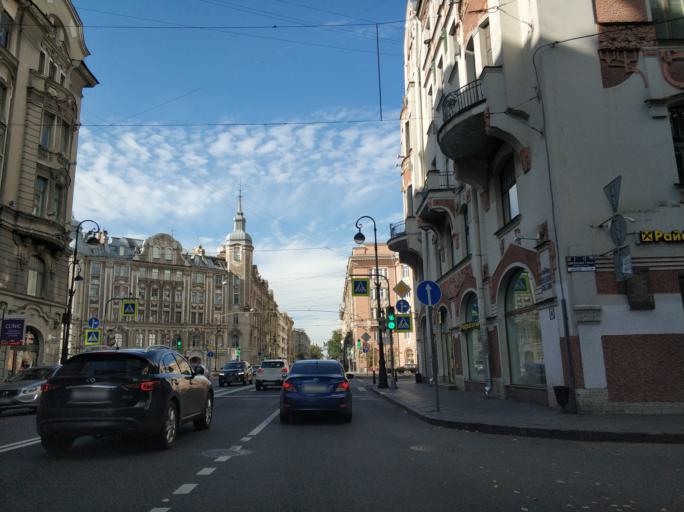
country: RU
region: St.-Petersburg
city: Petrogradka
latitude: 59.9594
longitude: 30.3179
